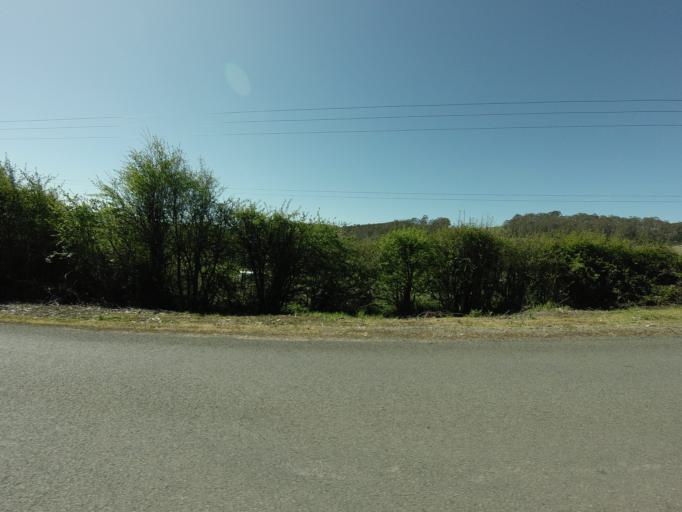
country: AU
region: Tasmania
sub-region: Derwent Valley
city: New Norfolk
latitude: -42.6211
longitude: 146.7187
